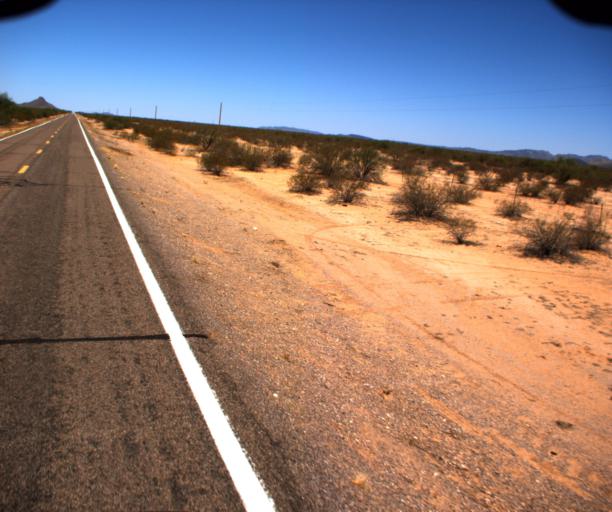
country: US
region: Arizona
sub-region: Pima County
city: Ajo
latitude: 32.1961
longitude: -112.4601
